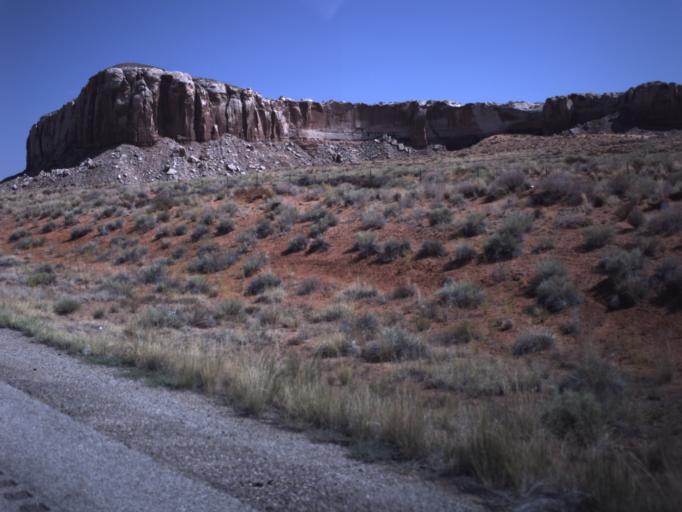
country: US
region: Utah
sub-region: San Juan County
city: Blanding
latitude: 37.2287
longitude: -109.6168
